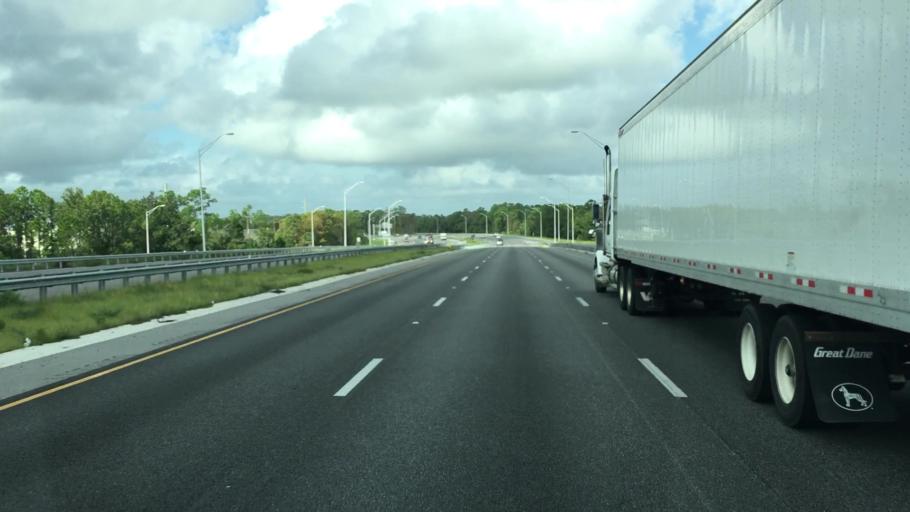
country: US
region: Florida
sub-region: Volusia County
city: Port Orange
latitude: 29.1078
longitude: -81.0294
